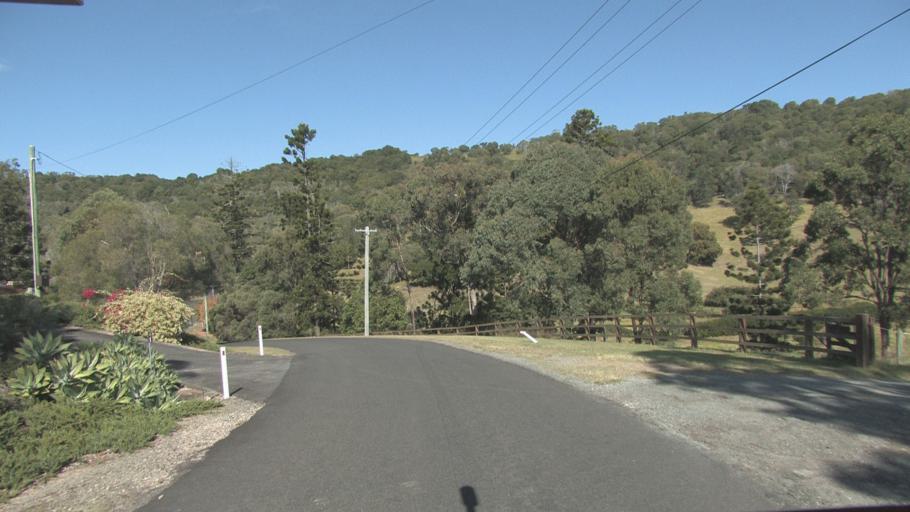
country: AU
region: Queensland
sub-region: Logan
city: Windaroo
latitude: -27.7430
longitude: 153.1720
